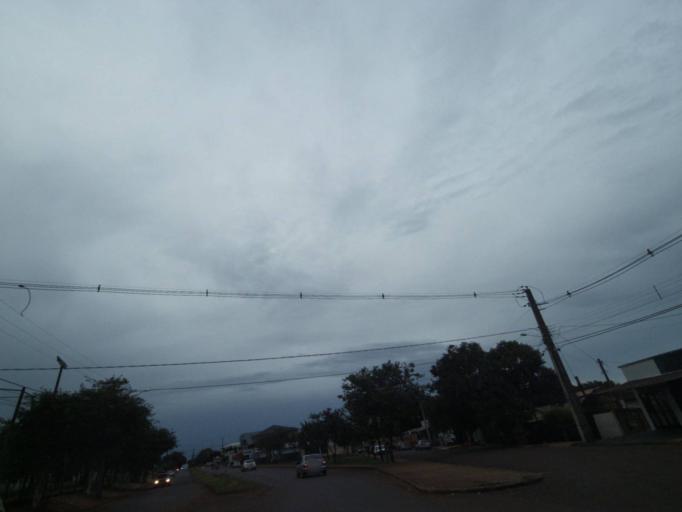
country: BR
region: Parana
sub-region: Campo Mourao
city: Campo Mourao
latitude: -24.0208
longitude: -52.3556
